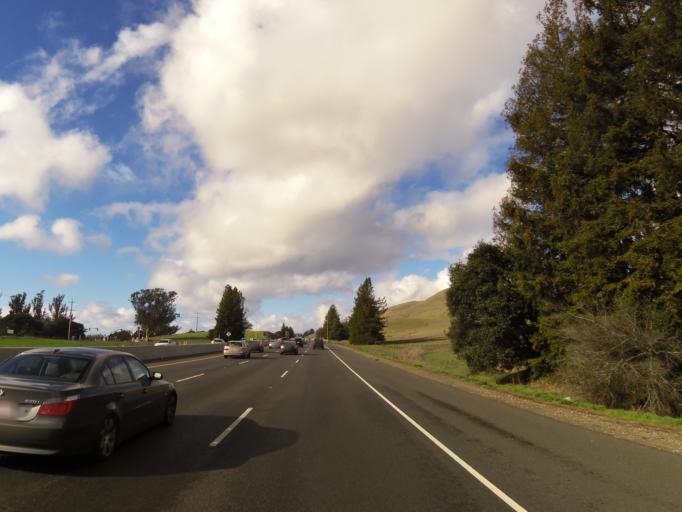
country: US
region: California
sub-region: Sonoma County
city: Penngrove
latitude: 38.2834
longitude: -122.6845
